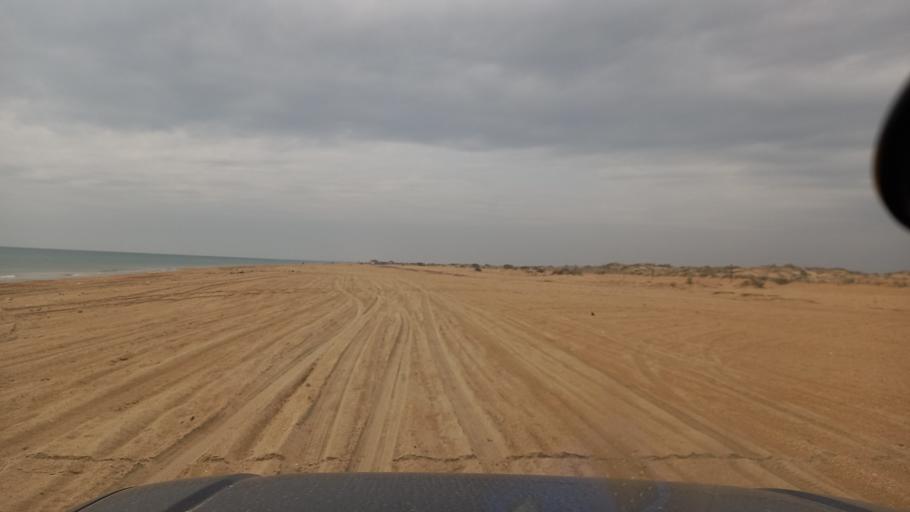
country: RU
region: Krasnodarskiy
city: Vityazevo
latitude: 44.9917
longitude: 37.2315
